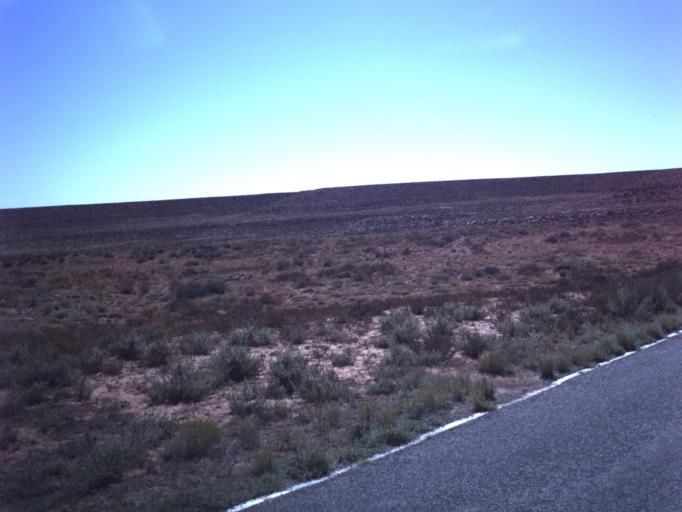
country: US
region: Arizona
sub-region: Navajo County
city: Kayenta
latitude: 37.1993
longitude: -109.8983
